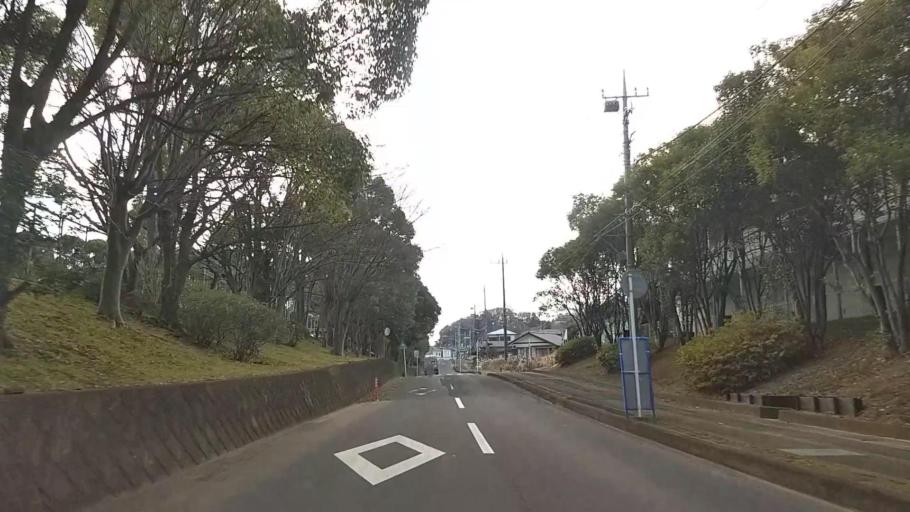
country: JP
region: Kanagawa
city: Isehara
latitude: 35.4097
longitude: 139.3153
